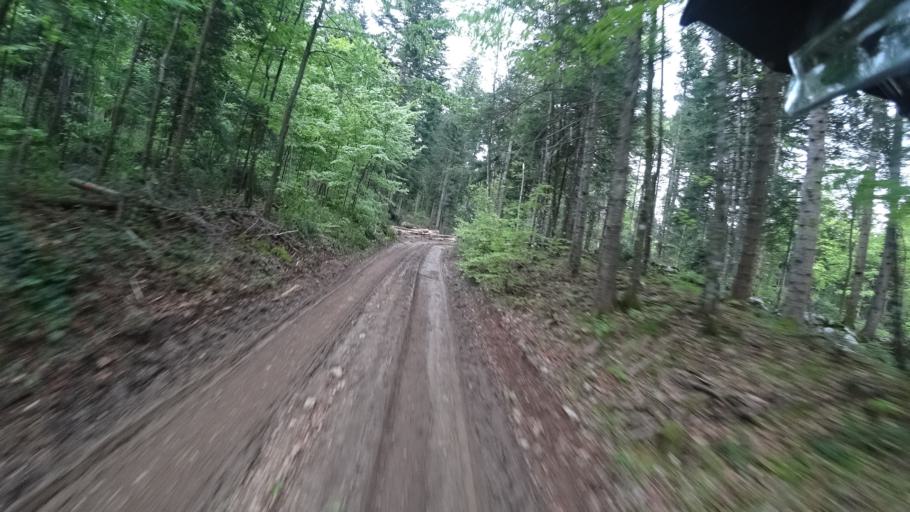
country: HR
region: Karlovacka
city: Plaski
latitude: 44.9509
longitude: 15.4151
